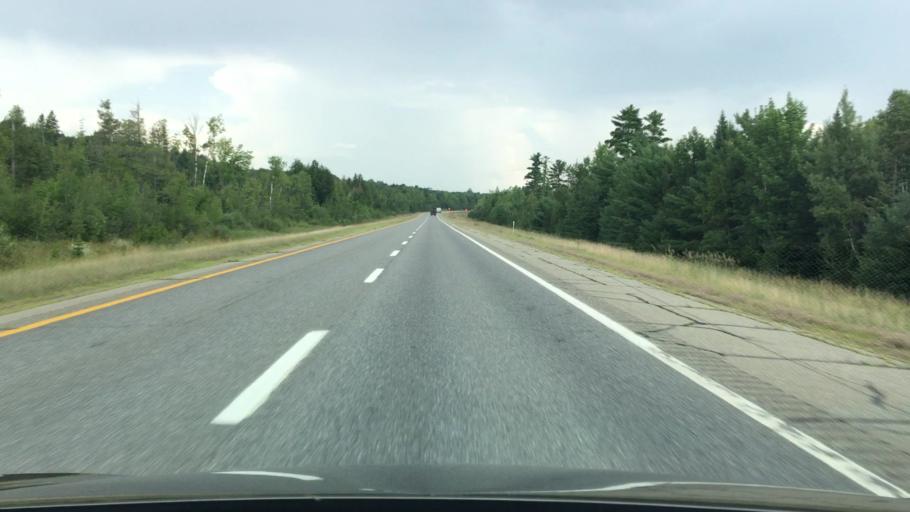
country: US
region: Maine
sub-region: Penobscot County
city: Medway
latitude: 45.5411
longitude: -68.5519
